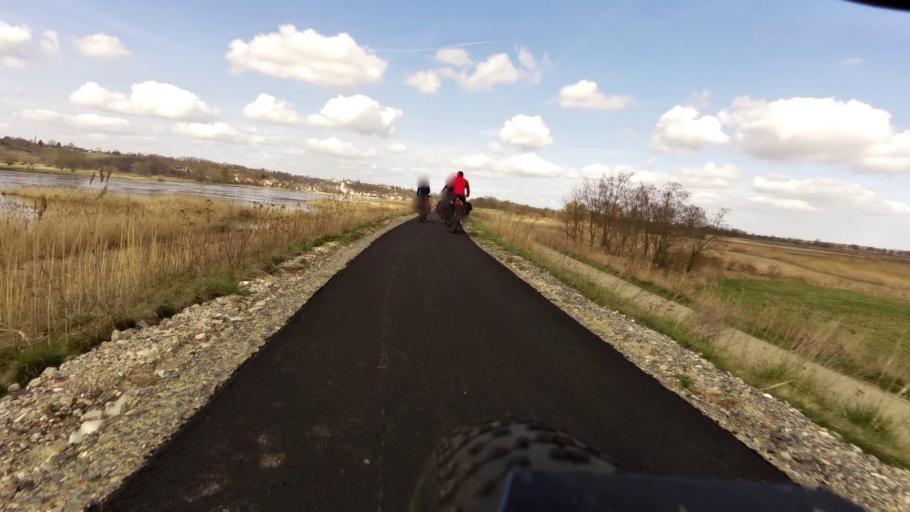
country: DE
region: Brandenburg
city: Lebus
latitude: 52.4150
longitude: 14.5494
